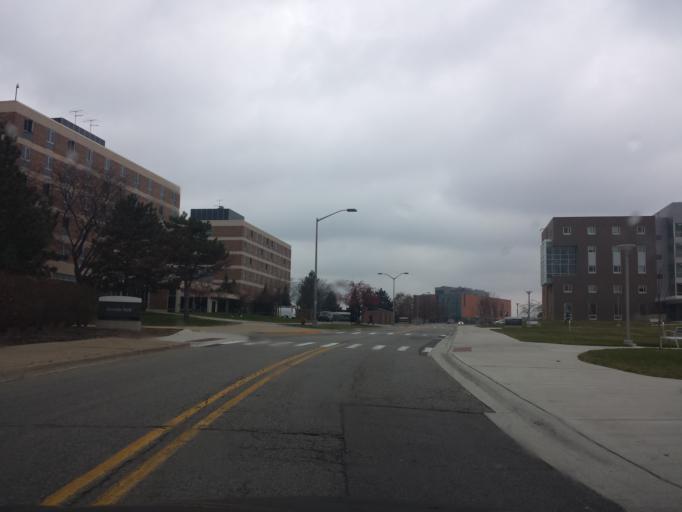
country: US
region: Michigan
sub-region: Oakland County
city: Auburn Hills
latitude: 42.6775
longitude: -83.2146
